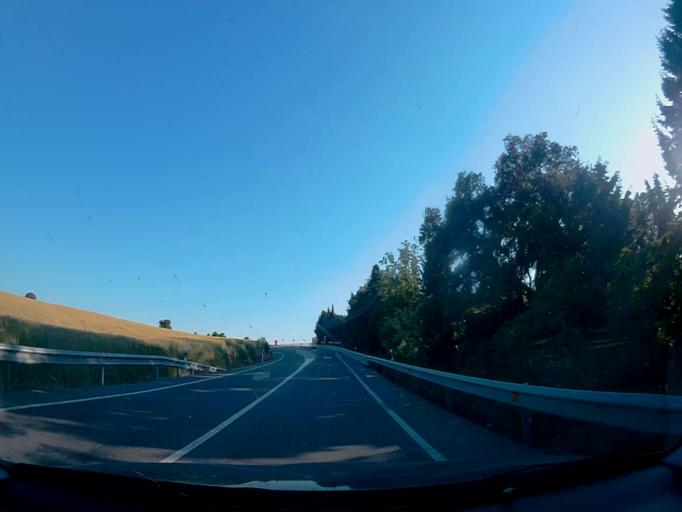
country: ES
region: Castille-La Mancha
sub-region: Province of Toledo
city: Escalona
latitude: 40.1235
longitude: -4.4087
